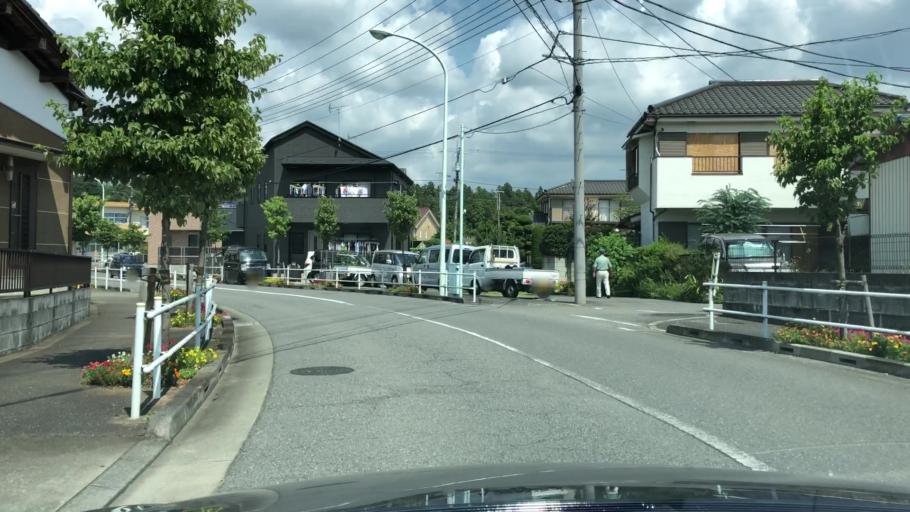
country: JP
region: Tokyo
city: Fussa
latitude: 35.7198
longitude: 139.2788
